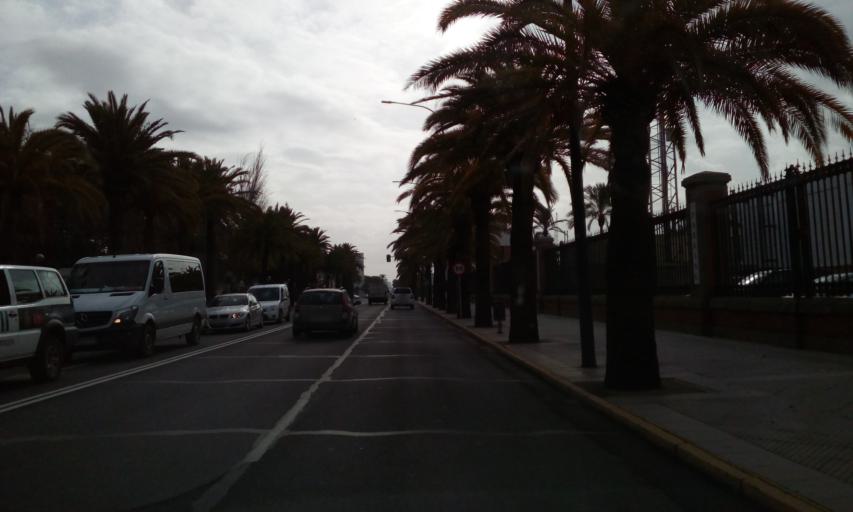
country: ES
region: Andalusia
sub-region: Provincia de Huelva
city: Huelva
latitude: 37.2562
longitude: -6.9597
